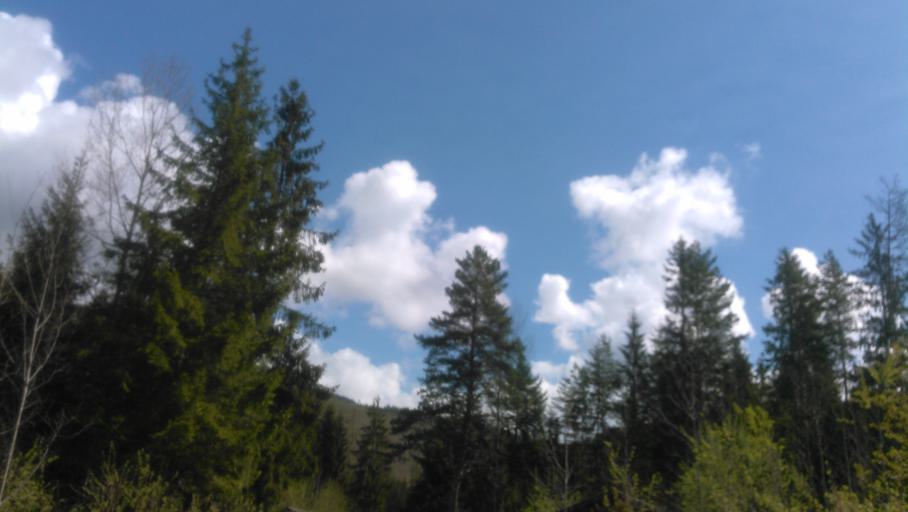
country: SK
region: Banskobystricky
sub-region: Okres Banska Bystrica
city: Brezno
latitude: 48.8696
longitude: 19.6004
